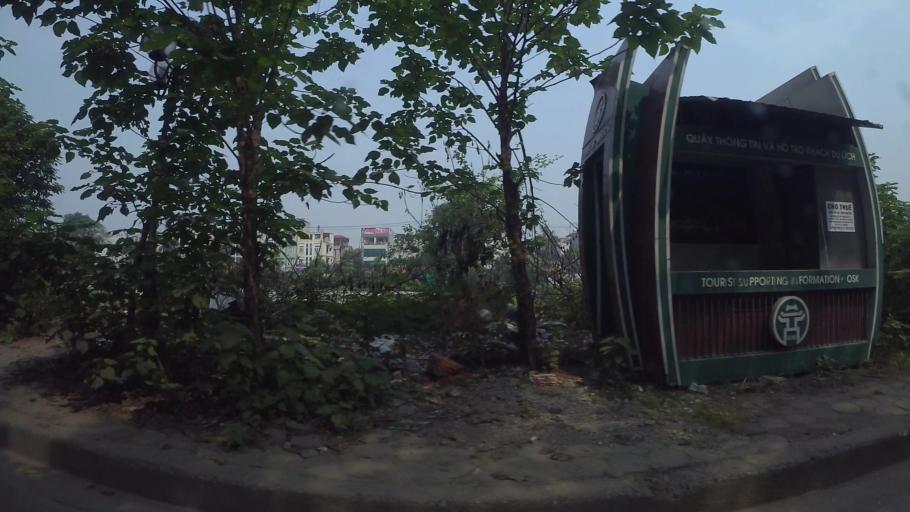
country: VN
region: Ha Noi
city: Van Dien
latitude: 20.9659
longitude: 105.8222
